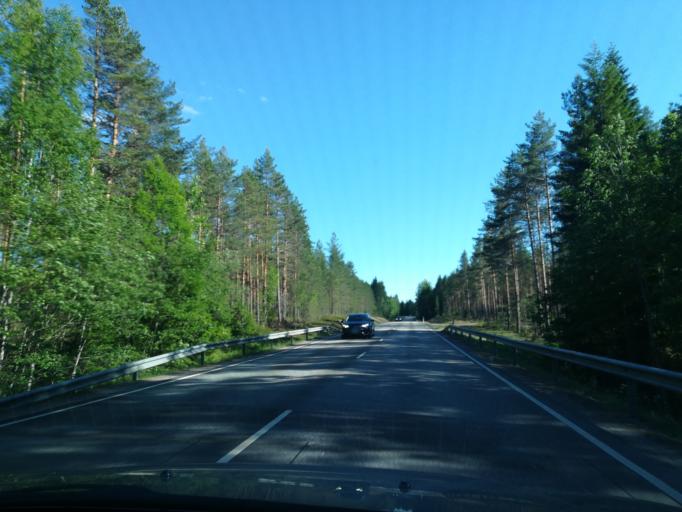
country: FI
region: South Karelia
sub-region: Imatra
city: Ruokolahti
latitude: 61.3825
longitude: 28.6544
